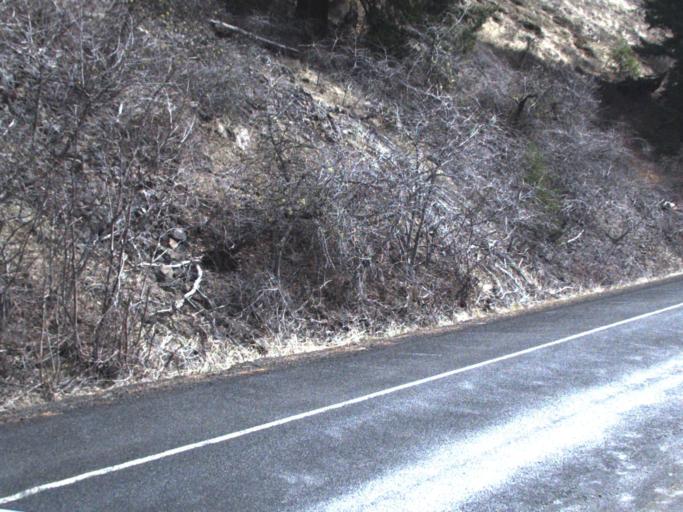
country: US
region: Washington
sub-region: Kittitas County
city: Cle Elum
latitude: 46.9617
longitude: -121.0827
